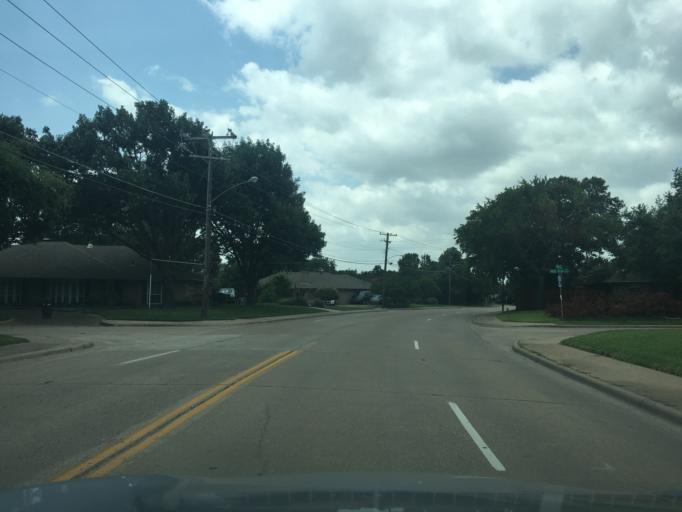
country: US
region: Texas
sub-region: Dallas County
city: Addison
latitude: 32.9245
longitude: -96.8288
